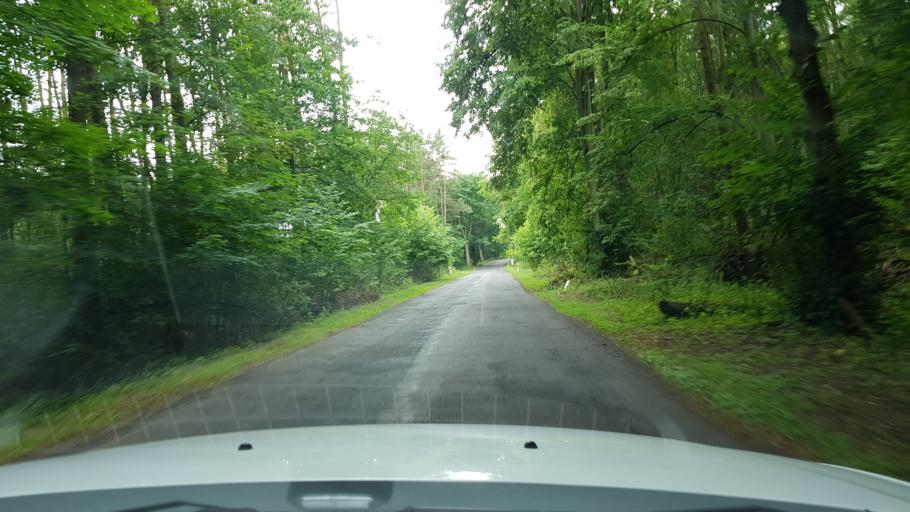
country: PL
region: West Pomeranian Voivodeship
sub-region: Powiat mysliborski
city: Boleszkowice
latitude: 52.6779
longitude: 14.5754
